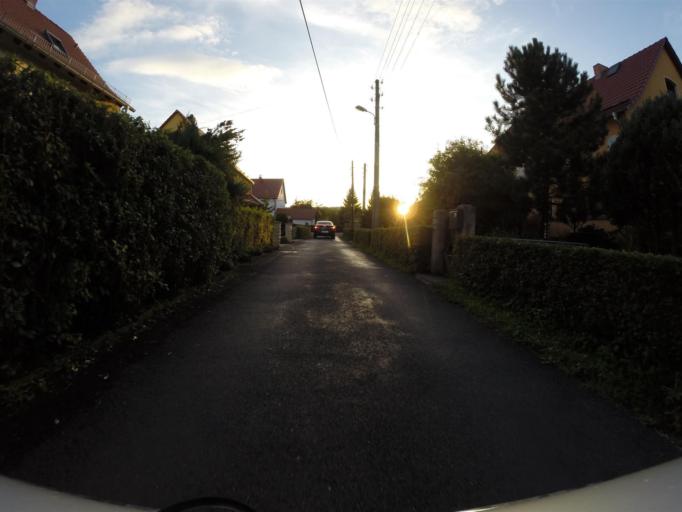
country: DE
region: Thuringia
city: Jena
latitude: 50.9069
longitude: 11.5754
